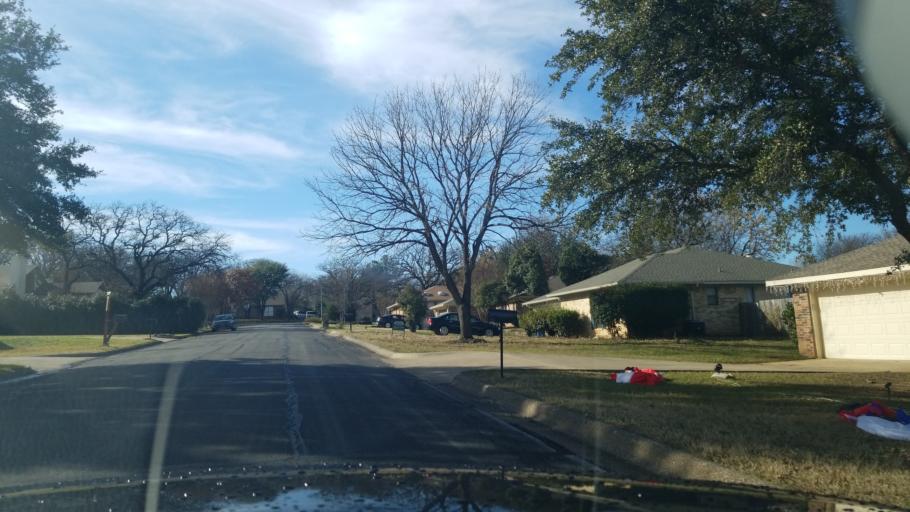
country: US
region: Texas
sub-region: Denton County
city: Corinth
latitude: 33.1547
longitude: -97.0716
